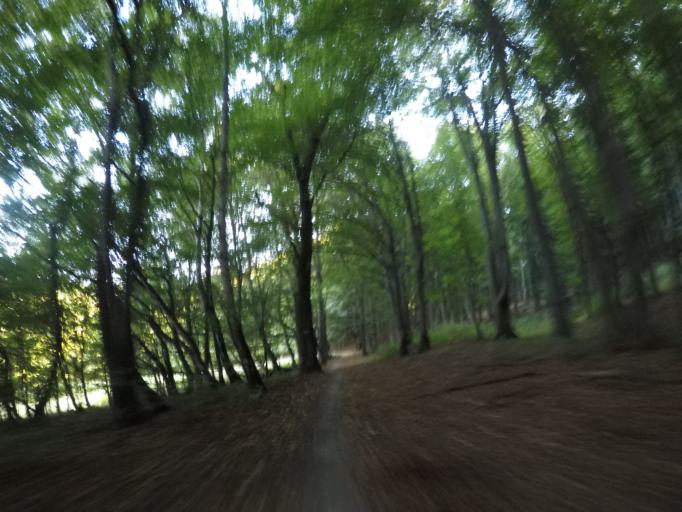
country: SK
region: Kosicky
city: Kosice
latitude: 48.7603
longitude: 21.1456
